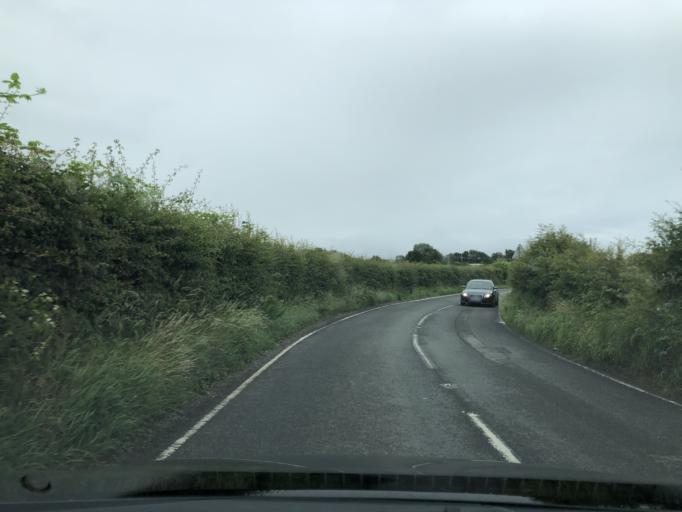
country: GB
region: Northern Ireland
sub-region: Down District
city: Dundrum
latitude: 54.2739
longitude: -5.7920
